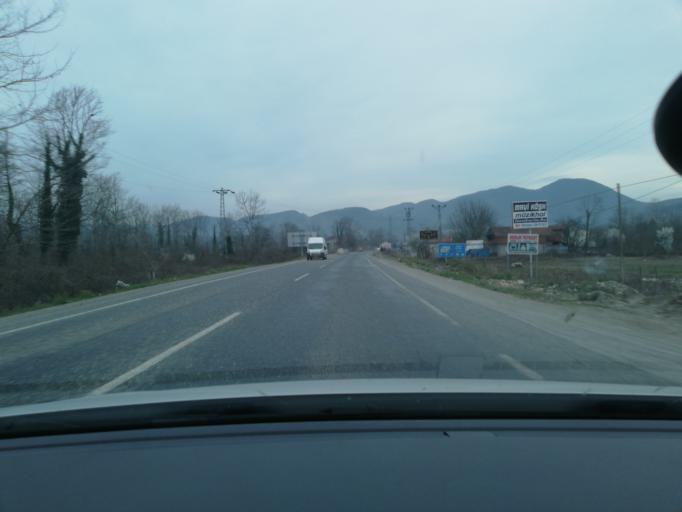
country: TR
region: Zonguldak
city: Gokcebey
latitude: 41.3015
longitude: 32.1130
